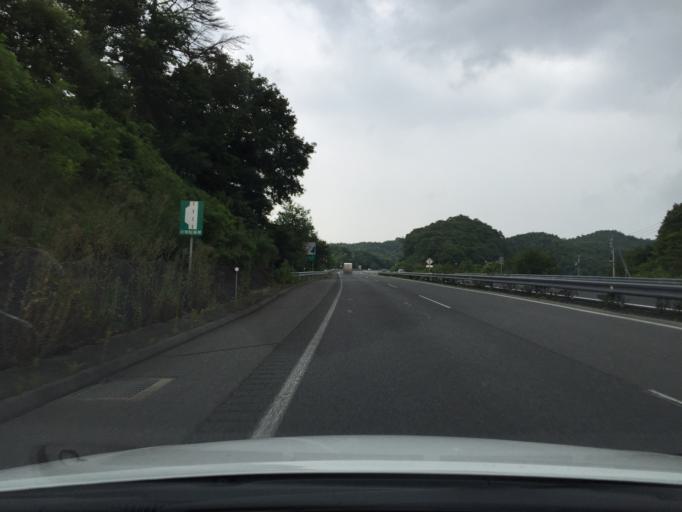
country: JP
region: Fukushima
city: Funehikimachi-funehiki
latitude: 37.2321
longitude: 140.6804
